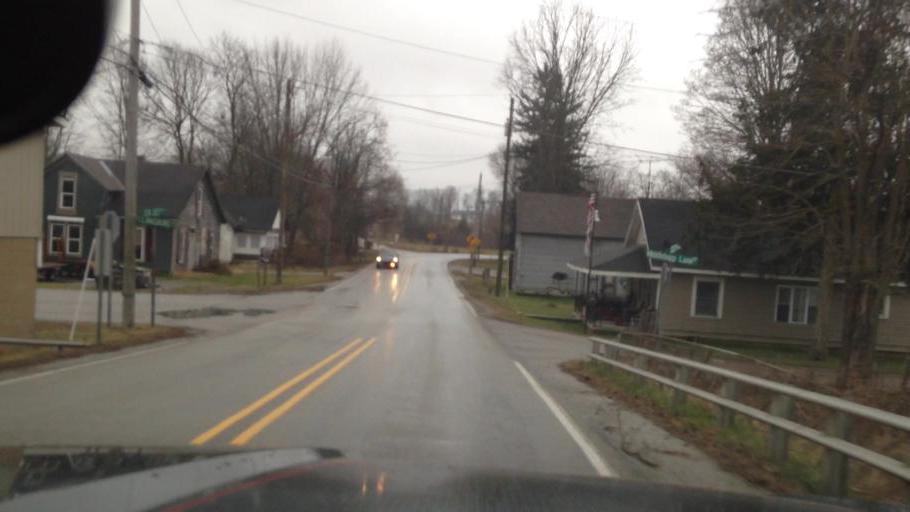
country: US
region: Ohio
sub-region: Preble County
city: New Paris
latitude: 39.8951
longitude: -84.8317
